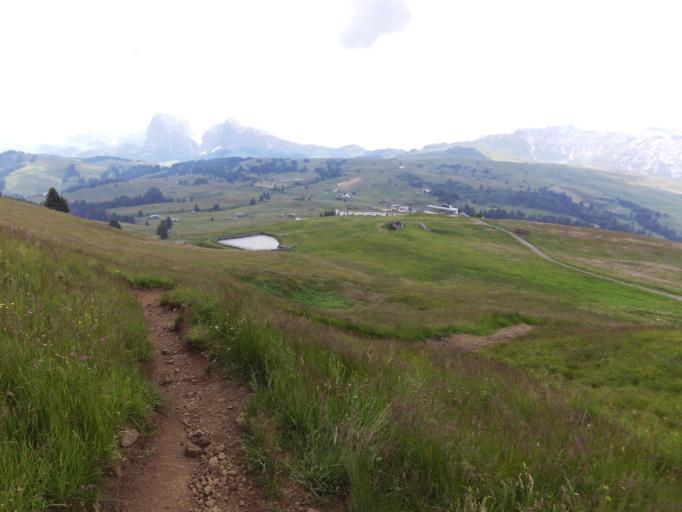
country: IT
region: Trentino-Alto Adige
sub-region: Bolzano
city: Siusi
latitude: 46.5464
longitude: 11.6126
